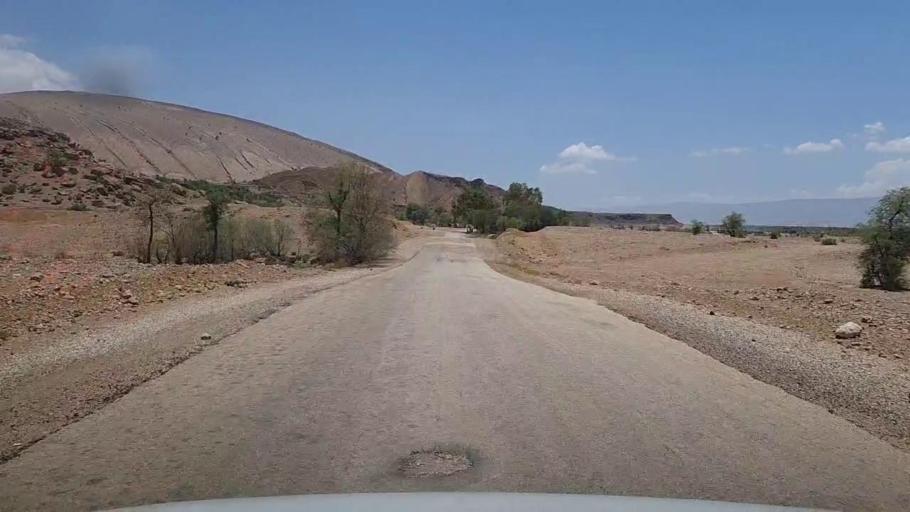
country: PK
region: Sindh
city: Bhan
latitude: 26.3044
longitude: 67.5358
